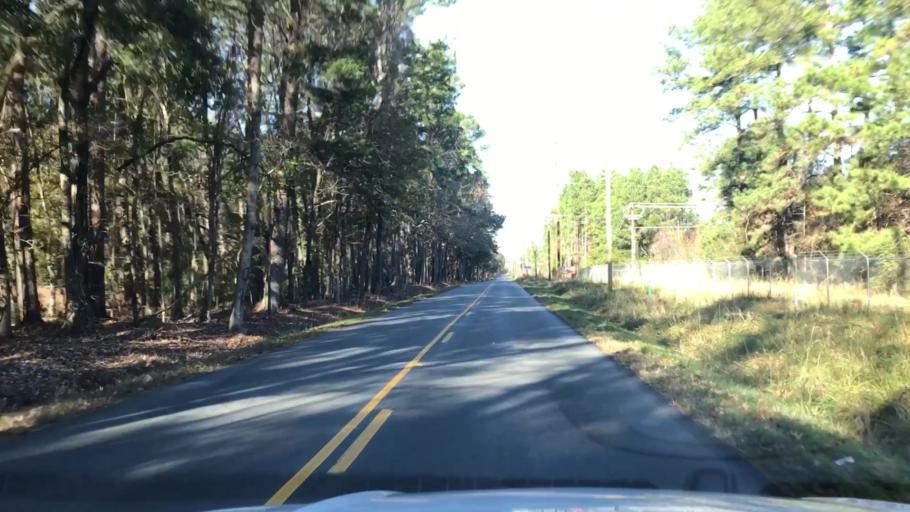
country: US
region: South Carolina
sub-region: Berkeley County
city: Ladson
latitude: 32.9872
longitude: -80.1125
